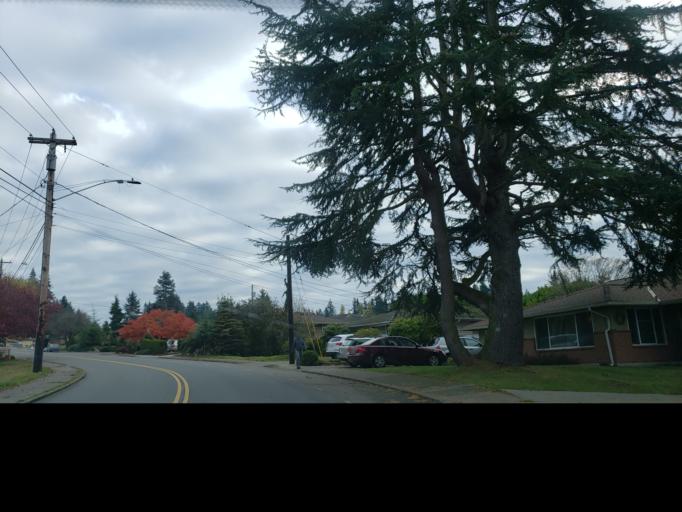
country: US
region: Washington
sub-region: Snohomish County
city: Everett
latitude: 47.9464
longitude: -122.2305
